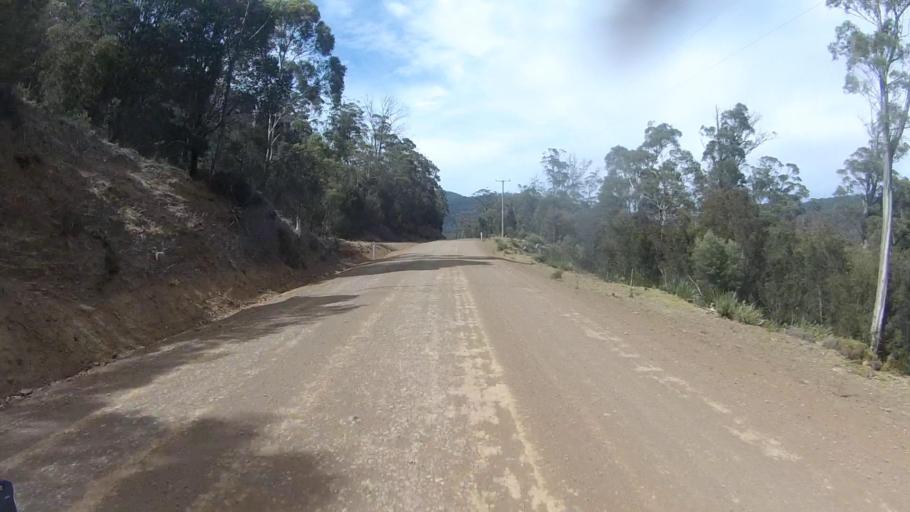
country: AU
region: Tasmania
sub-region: Sorell
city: Sorell
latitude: -42.6717
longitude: 147.8837
